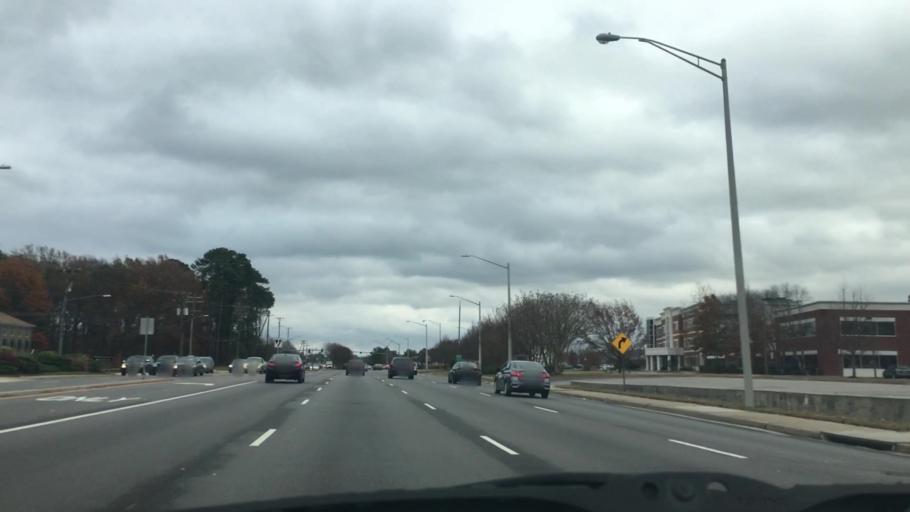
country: US
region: Virginia
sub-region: City of Chesapeake
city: Chesapeake
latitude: 36.8252
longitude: -76.1295
